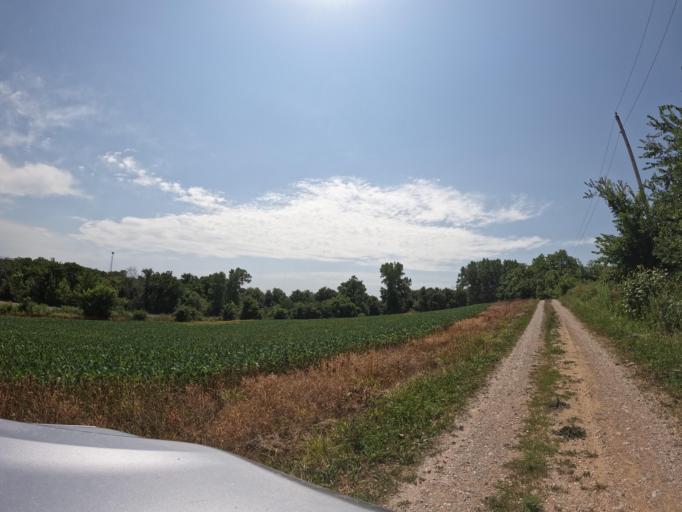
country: US
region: Iowa
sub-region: Appanoose County
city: Centerville
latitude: 40.7729
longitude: -92.9496
